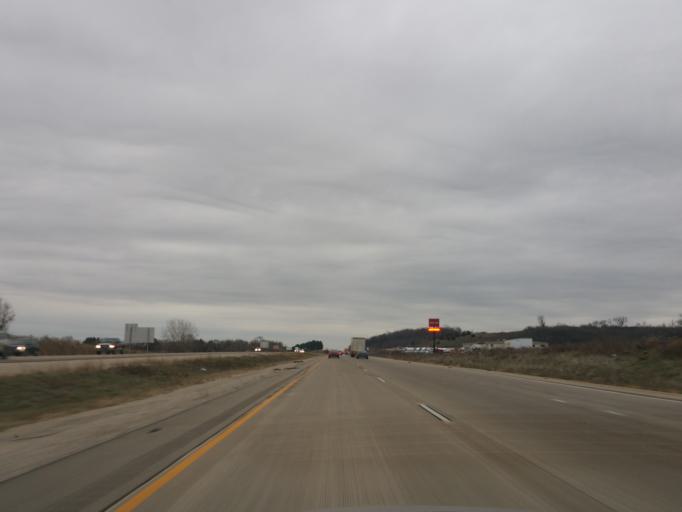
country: US
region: Wisconsin
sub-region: Saint Croix County
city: Roberts
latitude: 44.9577
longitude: -92.5554
